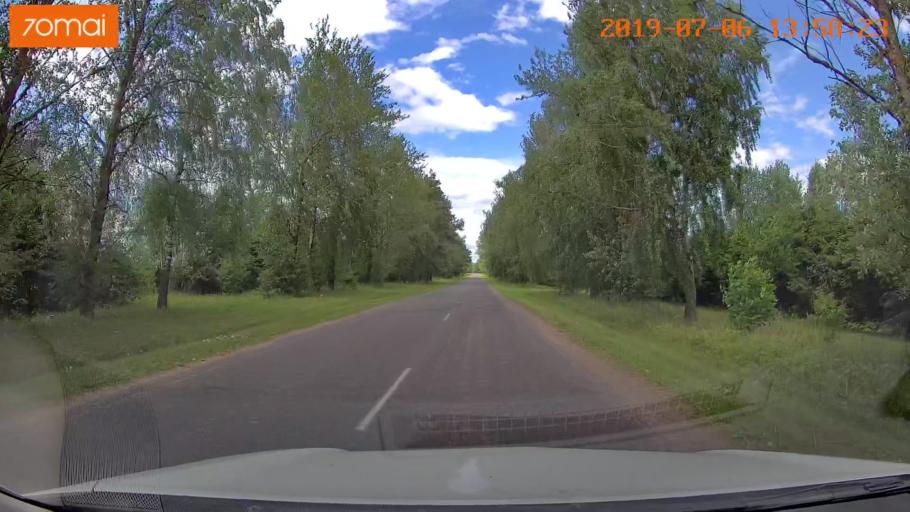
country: BY
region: Minsk
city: Ivyanyets
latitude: 53.7834
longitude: 26.8088
